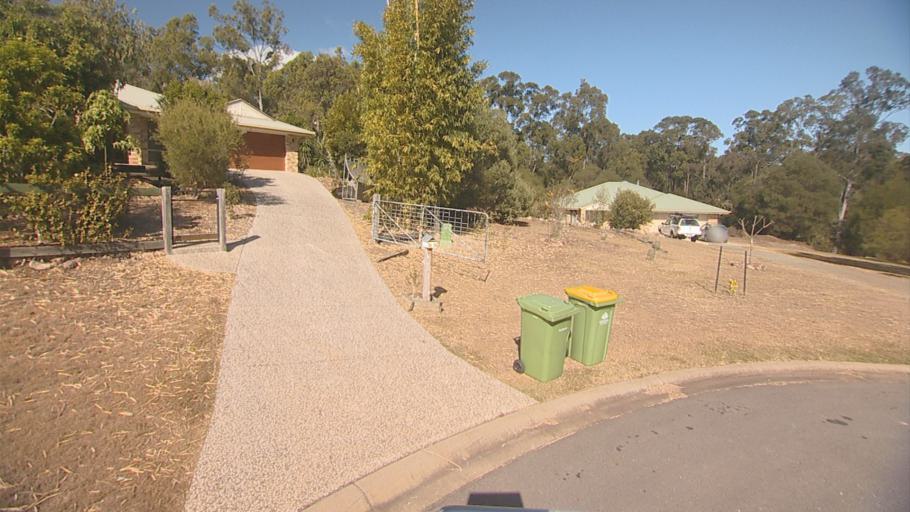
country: AU
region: Queensland
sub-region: Logan
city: Cedar Vale
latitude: -27.8917
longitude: 152.9982
